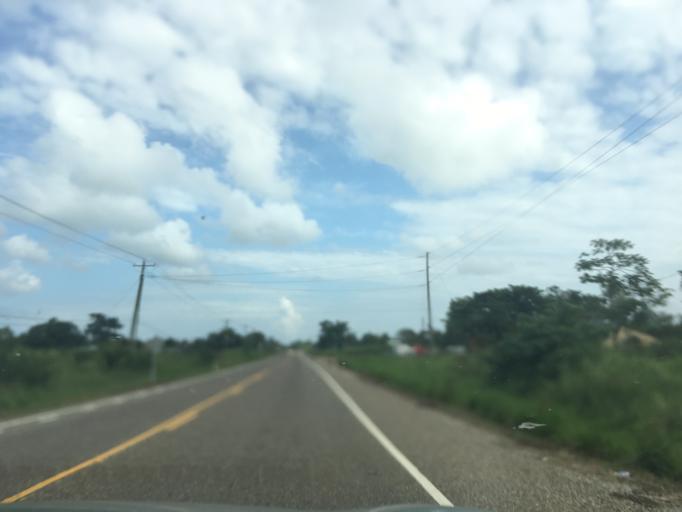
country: BZ
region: Stann Creek
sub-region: Dangriga
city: Dangriga
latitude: 16.9985
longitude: -88.3144
